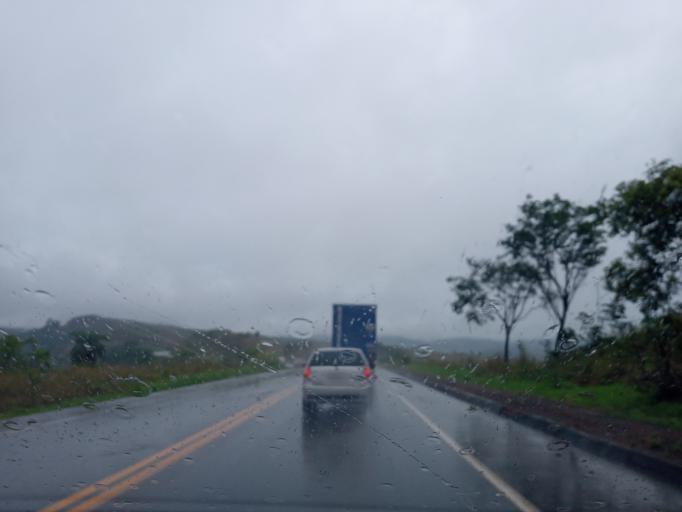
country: BR
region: Minas Gerais
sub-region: Luz
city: Luz
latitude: -19.7268
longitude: -45.8681
